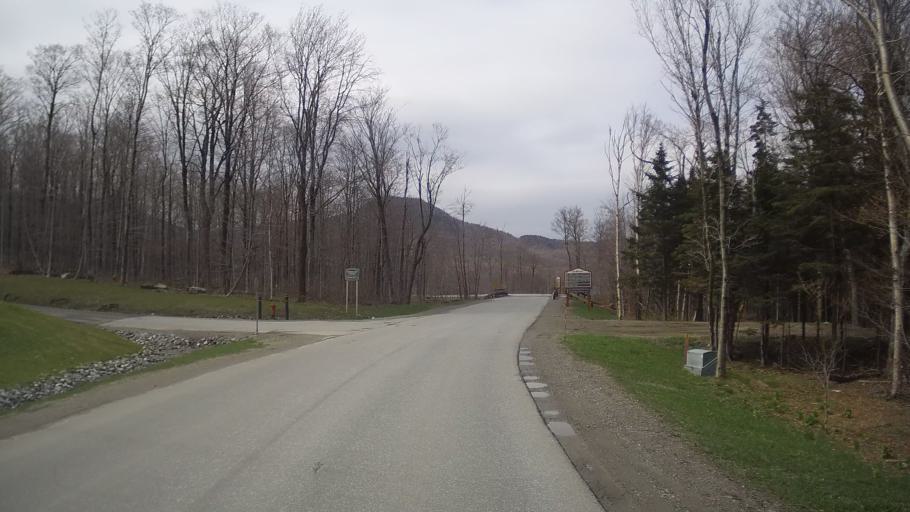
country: US
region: Vermont
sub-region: Franklin County
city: Richford
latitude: 44.9313
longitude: -72.4965
